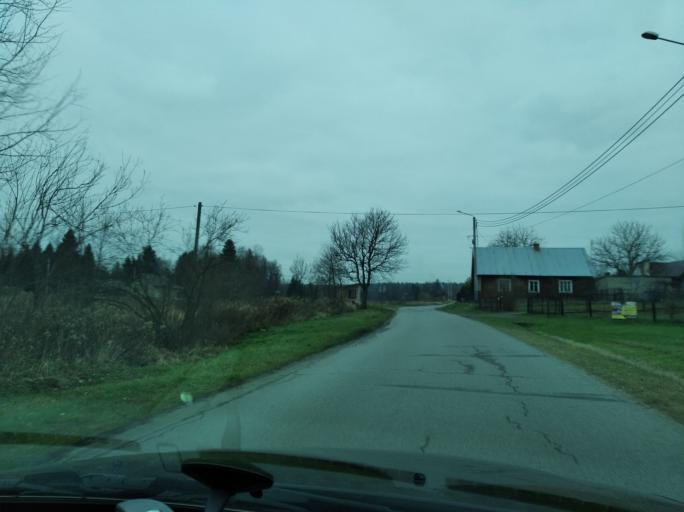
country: PL
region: Subcarpathian Voivodeship
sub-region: Powiat lancucki
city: Brzoza Stadnicka
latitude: 50.2023
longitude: 22.2948
